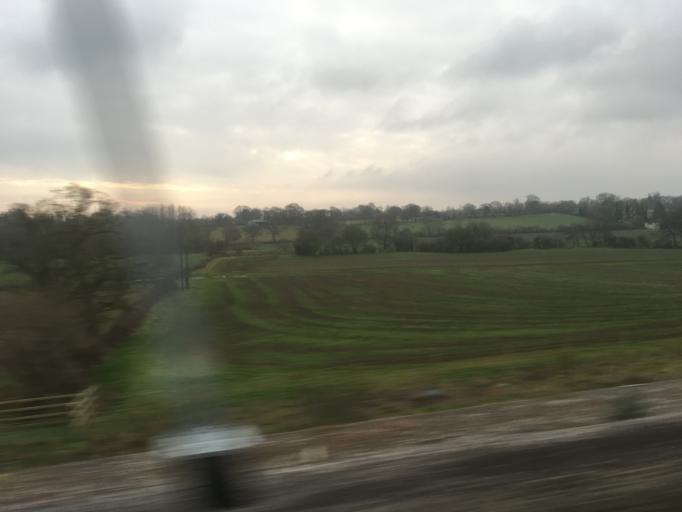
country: GB
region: England
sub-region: Wiltshire
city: Malmesbury
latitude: 51.5499
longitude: -2.0854
